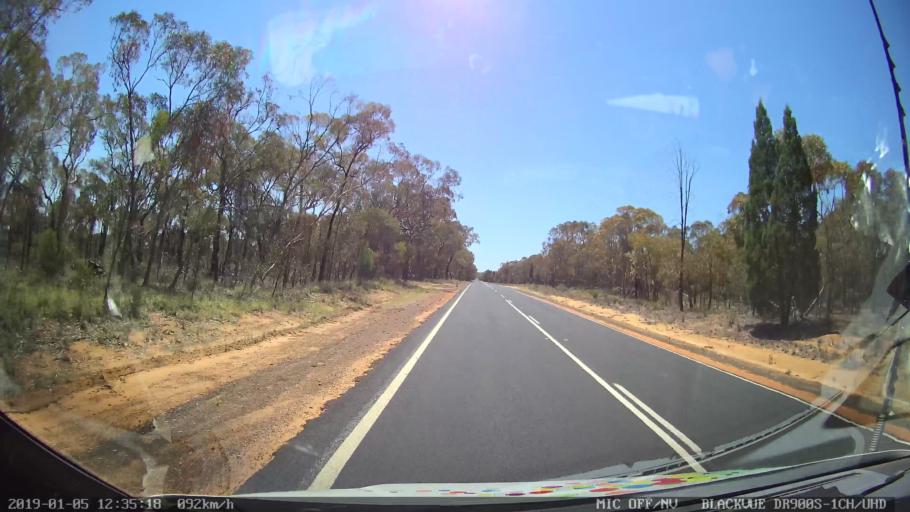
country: AU
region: New South Wales
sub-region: Warrumbungle Shire
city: Coonabarabran
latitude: -31.2100
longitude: 149.4235
